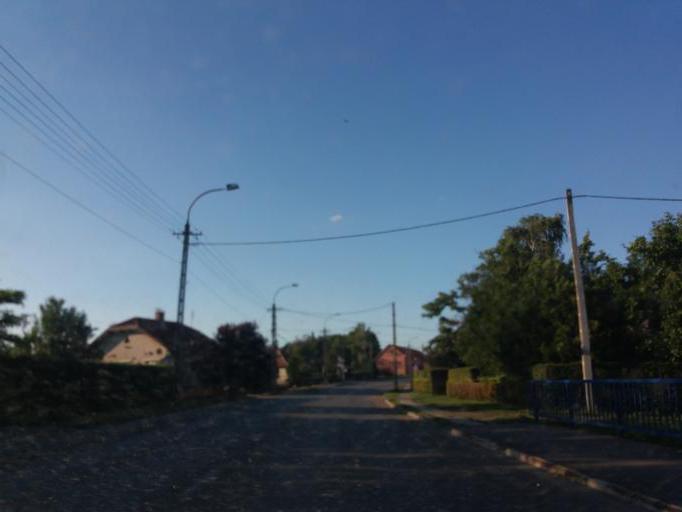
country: HU
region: Fejer
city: Martonvasar
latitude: 47.3124
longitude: 18.7873
